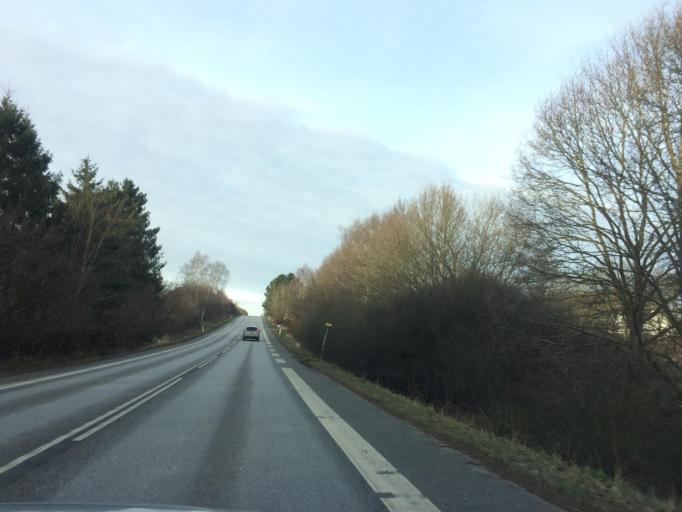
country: DK
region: Capital Region
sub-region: Fredensborg Kommune
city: Fredensborg
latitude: 55.9573
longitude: 12.4138
